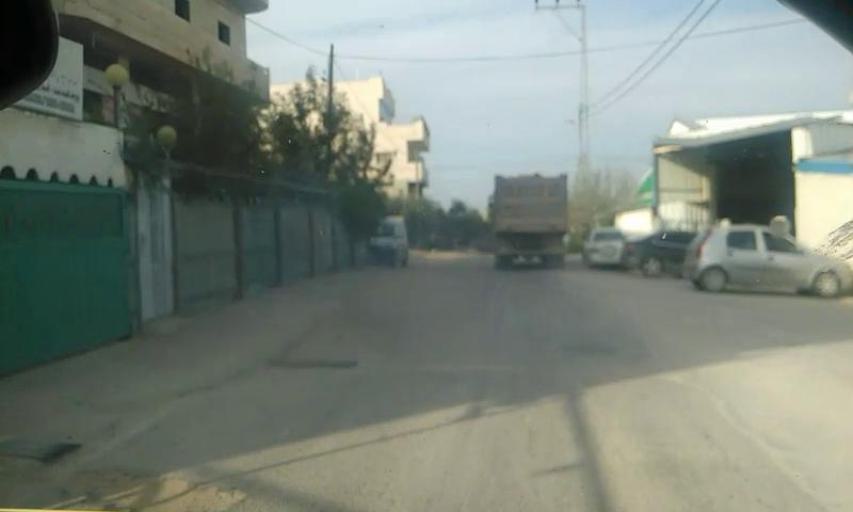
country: PS
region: West Bank
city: Bayt Ula
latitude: 31.5878
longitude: 35.0251
